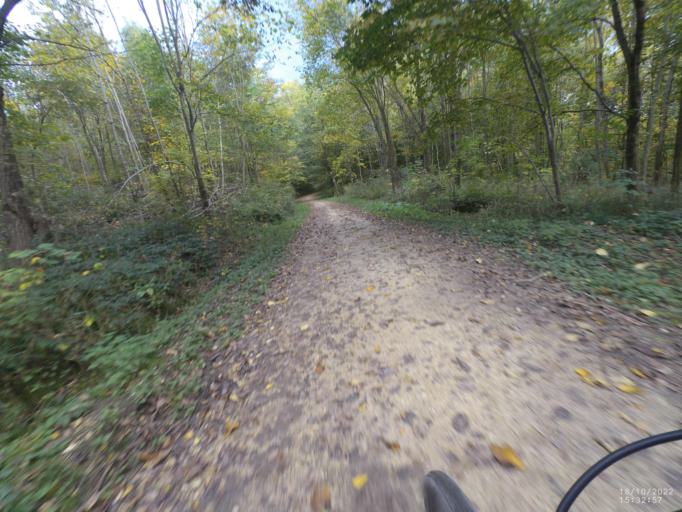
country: DE
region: Baden-Wuerttemberg
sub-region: Regierungsbezirk Stuttgart
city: Sussen
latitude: 48.7079
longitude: 9.7720
